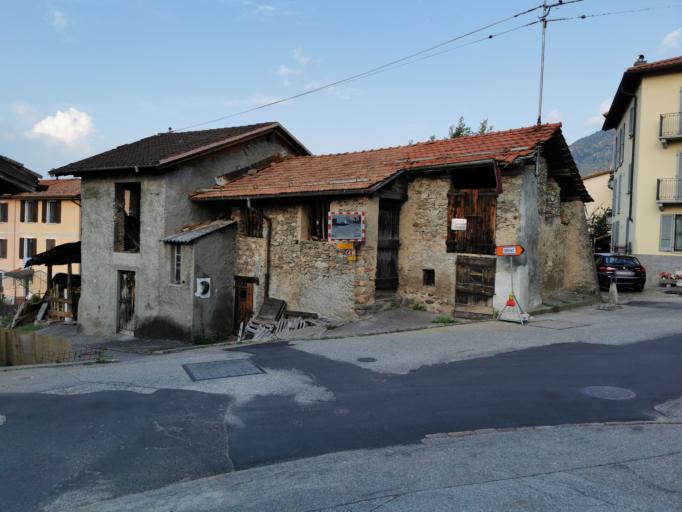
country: CH
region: Ticino
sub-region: Lugano District
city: Gravesano
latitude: 46.0469
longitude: 8.9006
